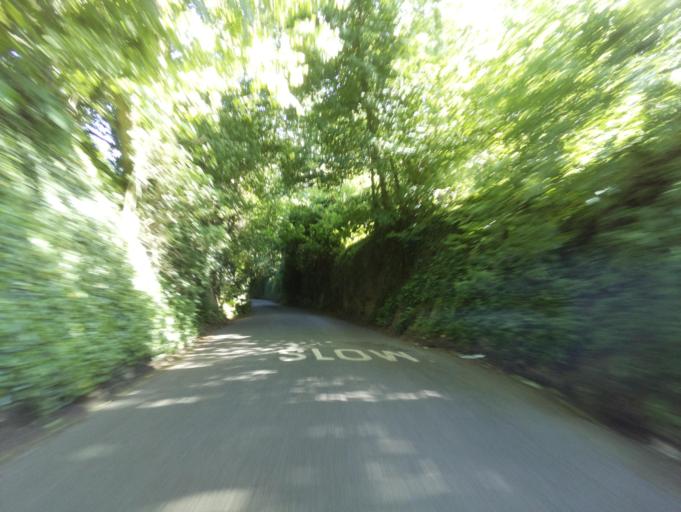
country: GB
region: England
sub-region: Somerset
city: Yeovil
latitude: 50.9380
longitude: -2.6019
